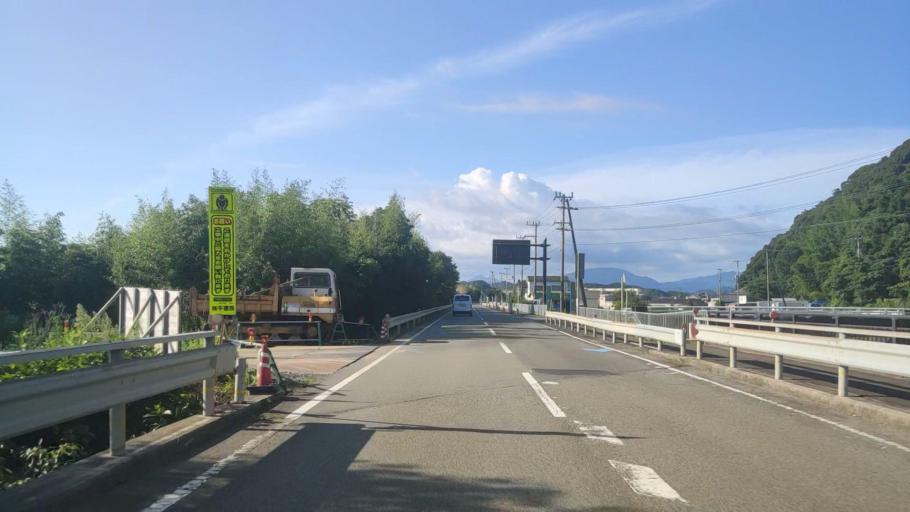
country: JP
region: Wakayama
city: Tanabe
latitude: 33.6695
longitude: 135.4081
